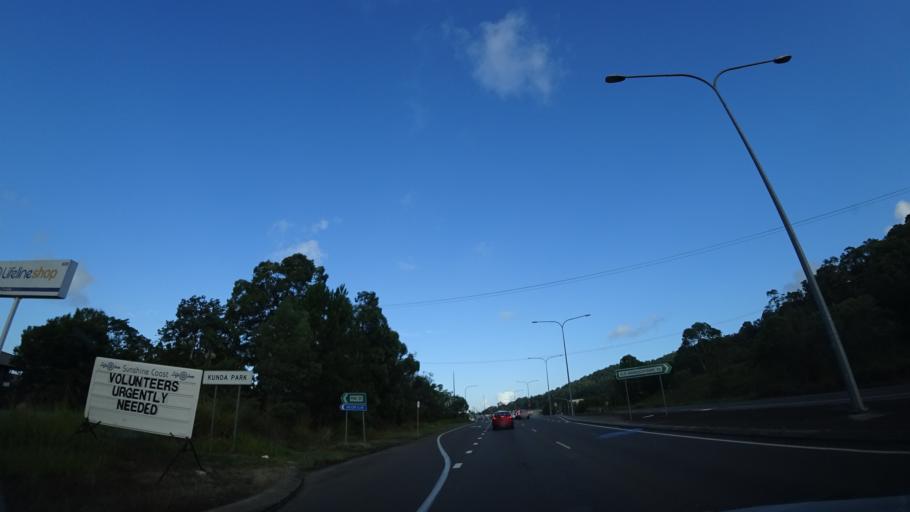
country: AU
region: Queensland
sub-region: Sunshine Coast
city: Buderim
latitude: -26.6621
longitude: 153.0336
